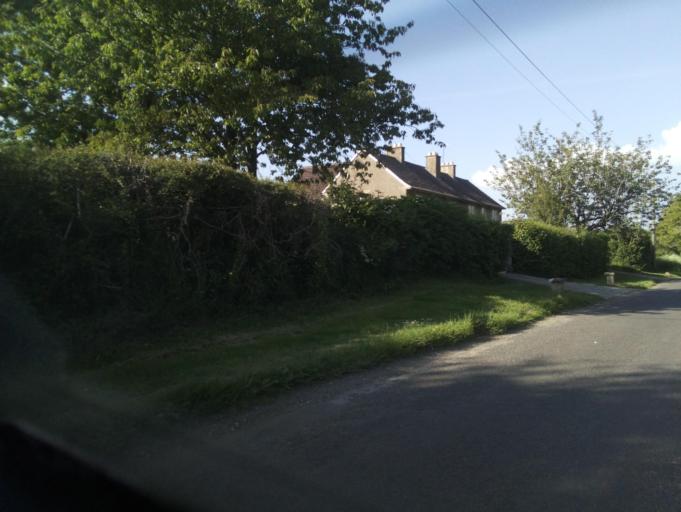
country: GB
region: England
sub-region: Wiltshire
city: Biddestone
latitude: 51.4750
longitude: -2.1795
